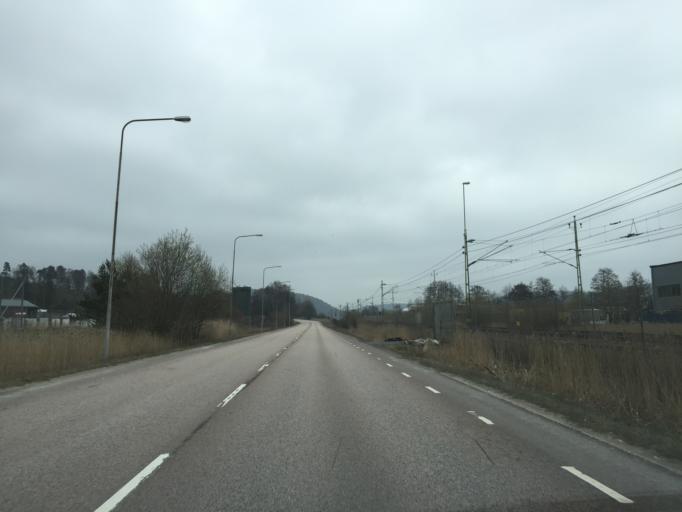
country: SE
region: Vaestra Goetaland
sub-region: Partille Kommun
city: Partille
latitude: 57.7449
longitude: 12.1240
